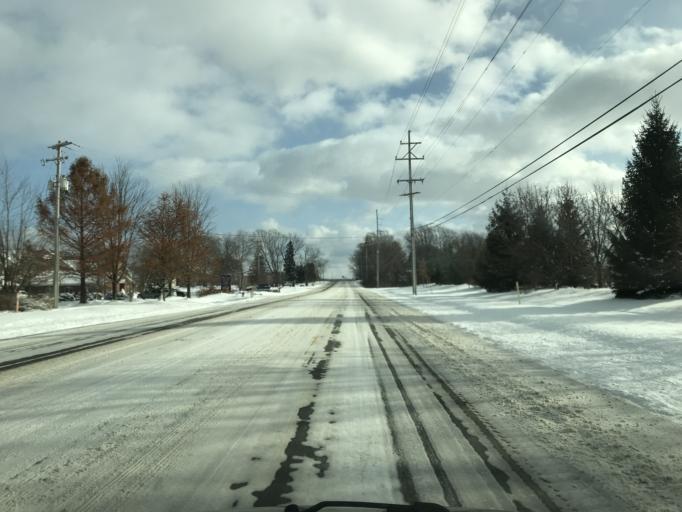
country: US
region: Michigan
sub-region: Kent County
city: Byron Center
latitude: 42.8264
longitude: -85.6952
